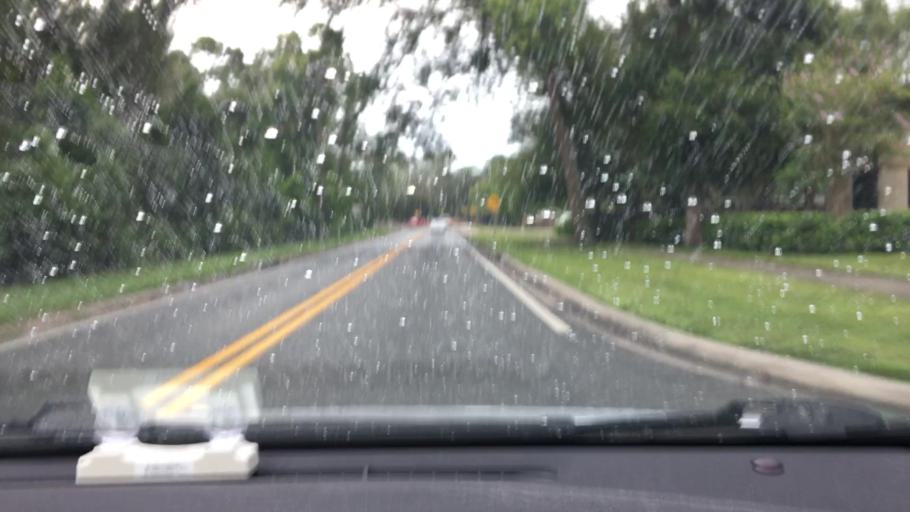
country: US
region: Florida
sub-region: Seminole County
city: Casselberry
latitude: 28.6743
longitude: -81.3459
